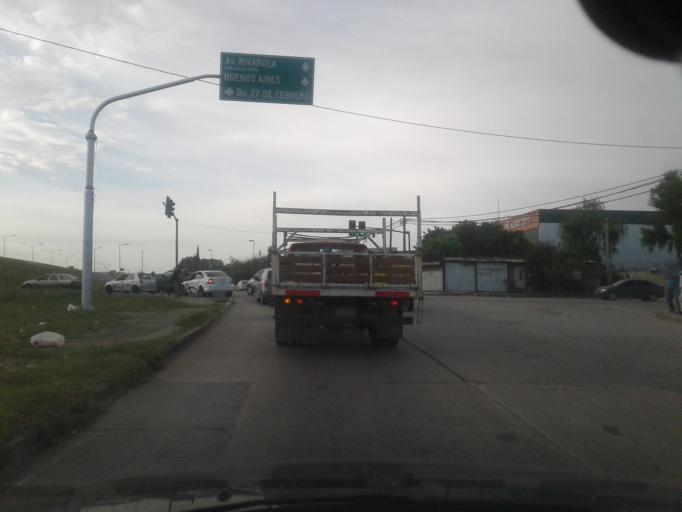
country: AR
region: Santa Fe
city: Perez
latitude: -32.9593
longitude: -60.7218
